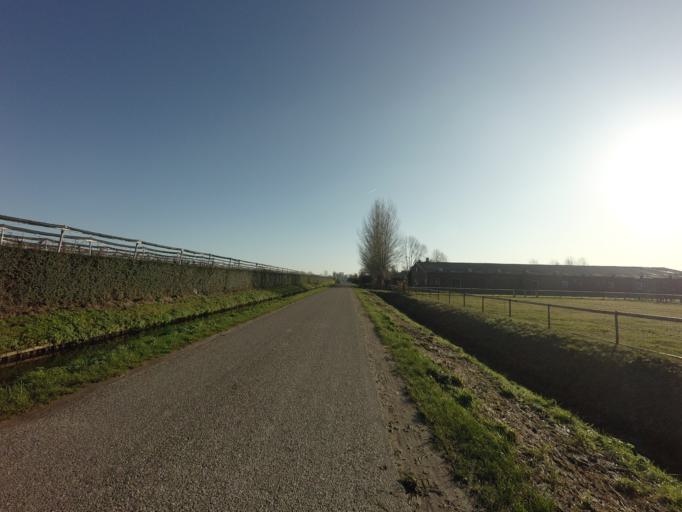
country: NL
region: Gelderland
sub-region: Gemeente Neerijnen
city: Neerijnen
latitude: 51.7907
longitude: 5.3115
